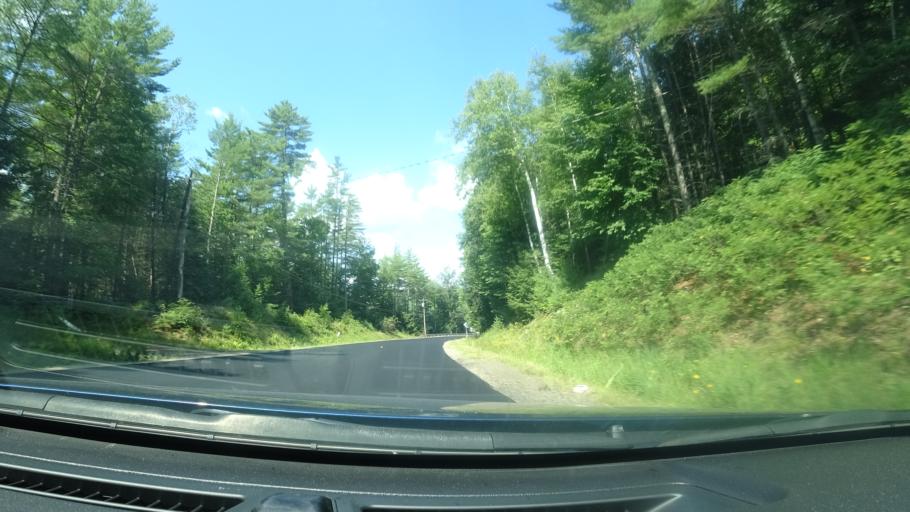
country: US
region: New York
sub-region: Warren County
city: Warrensburg
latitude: 43.6523
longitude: -73.8288
